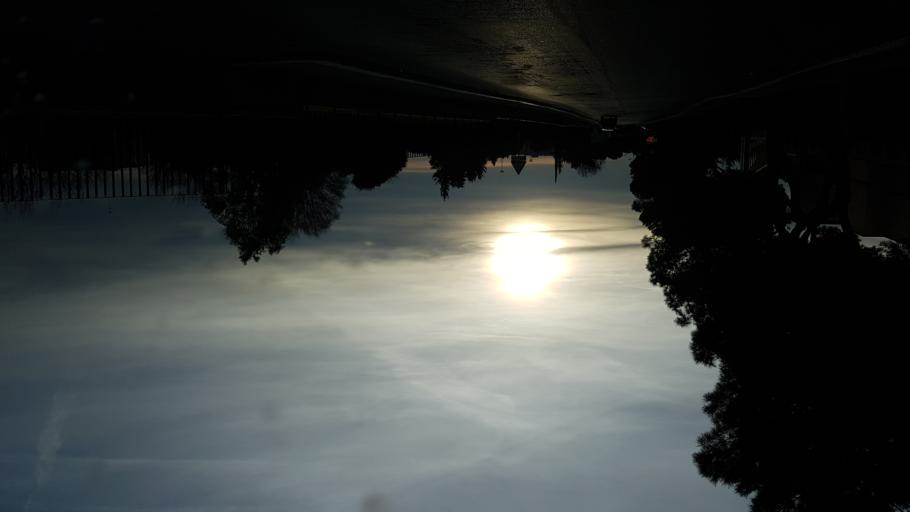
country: IT
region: Apulia
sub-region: Provincia di Brindisi
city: Brindisi
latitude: 40.6302
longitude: 17.9497
